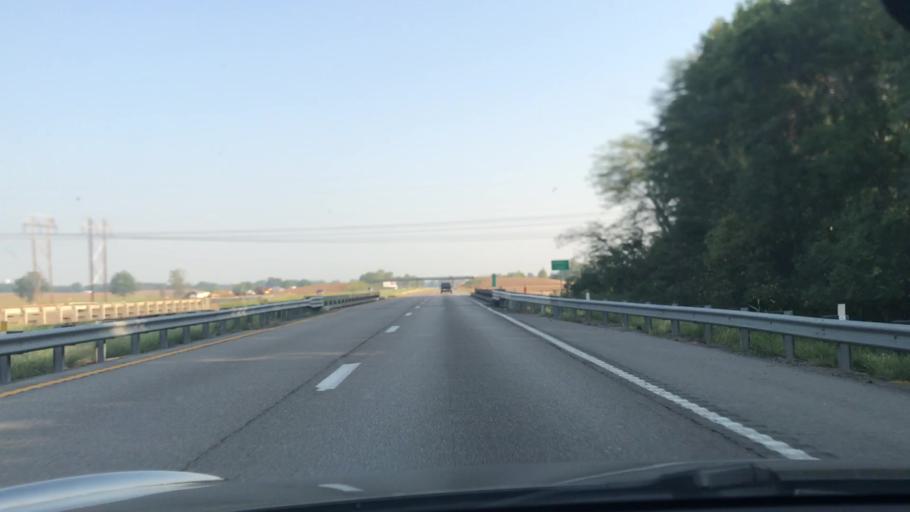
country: US
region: Missouri
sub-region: Scott County
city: Scott City
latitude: 37.1783
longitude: -89.5374
